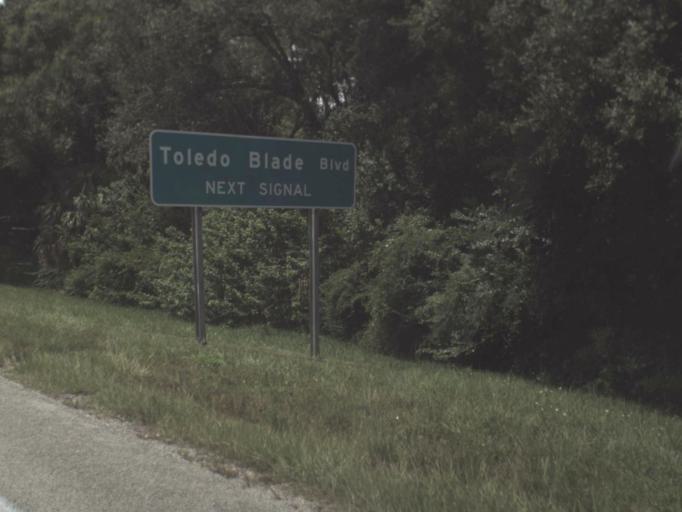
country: US
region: Florida
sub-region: Sarasota County
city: North Port
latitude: 27.0184
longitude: -82.1616
